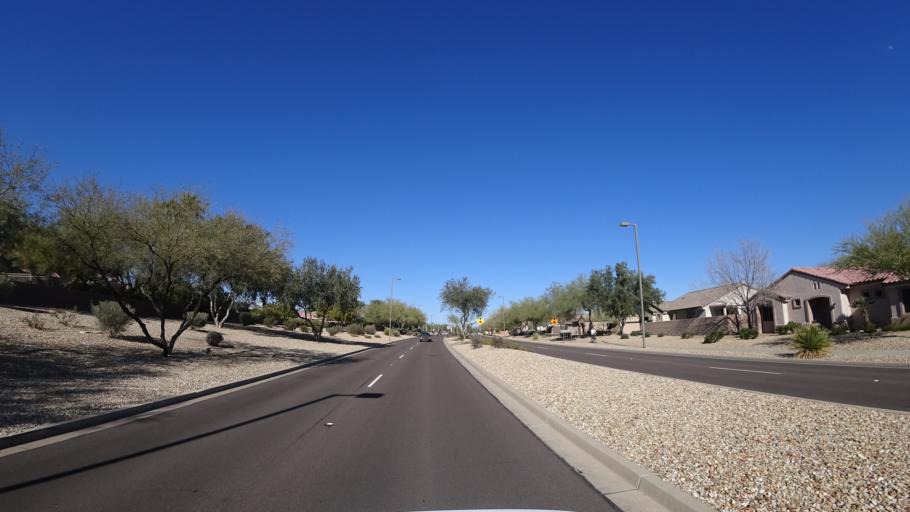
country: US
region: Arizona
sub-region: Maricopa County
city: Sun City West
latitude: 33.6566
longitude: -112.4039
